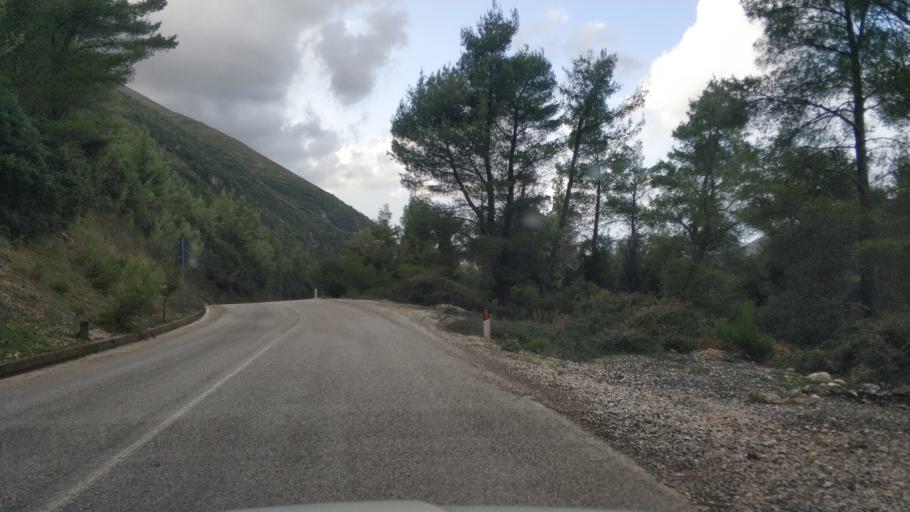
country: AL
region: Vlore
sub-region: Rrethi i Vlores
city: Orikum
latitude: 40.2540
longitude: 19.5348
